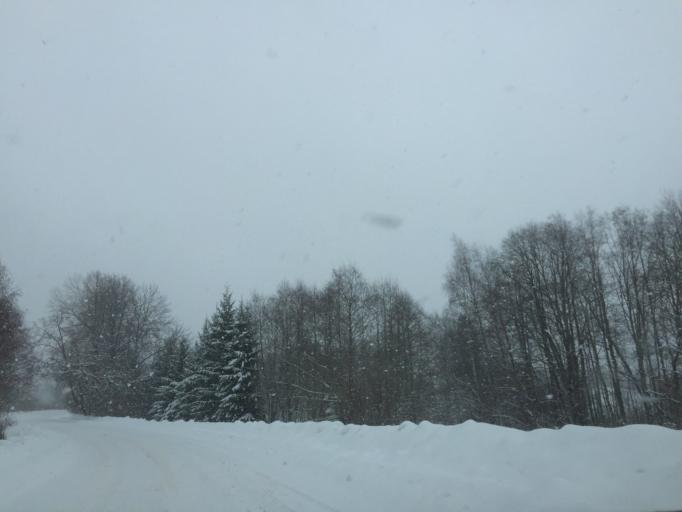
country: LV
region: Amatas Novads
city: Drabesi
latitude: 57.0684
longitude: 25.3268
